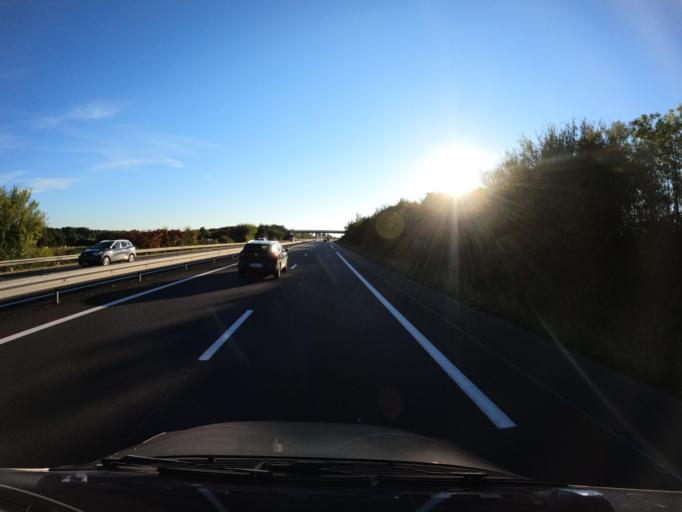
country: FR
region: Pays de la Loire
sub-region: Departement de la Vendee
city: Saint-Fulgent
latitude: 46.8234
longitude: -1.1767
